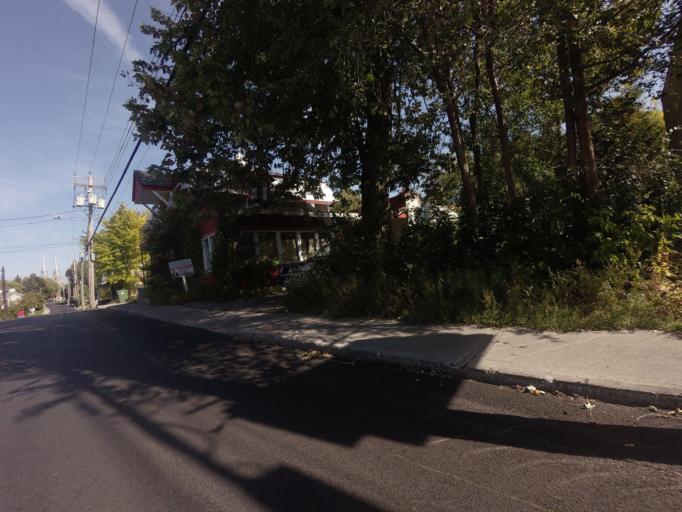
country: CA
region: Quebec
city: Kirkland
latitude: 45.4771
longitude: -73.8742
